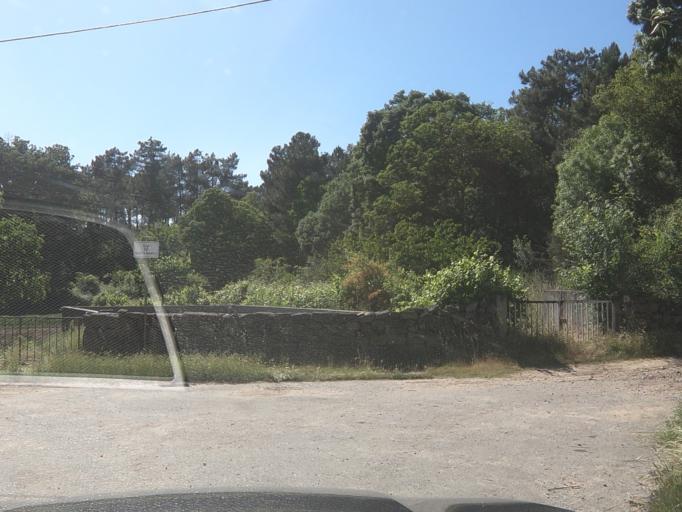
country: PT
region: Vila Real
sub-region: Vila Real
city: Vila Real
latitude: 41.2986
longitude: -7.6776
